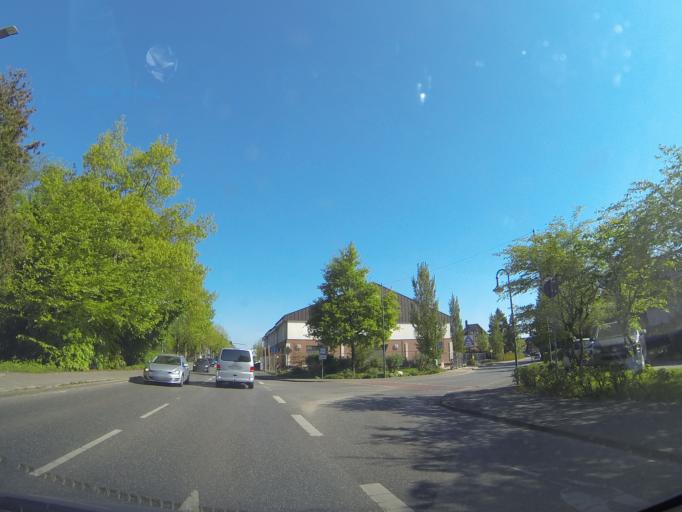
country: DE
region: Schleswig-Holstein
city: Halstenbek
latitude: 53.6338
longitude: 9.8375
